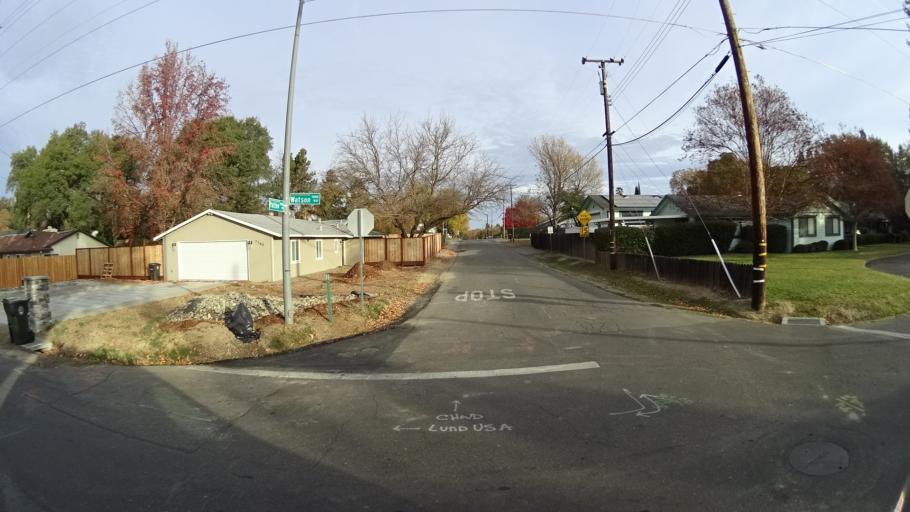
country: US
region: California
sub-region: Sacramento County
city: Citrus Heights
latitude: 38.7076
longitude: -121.2765
